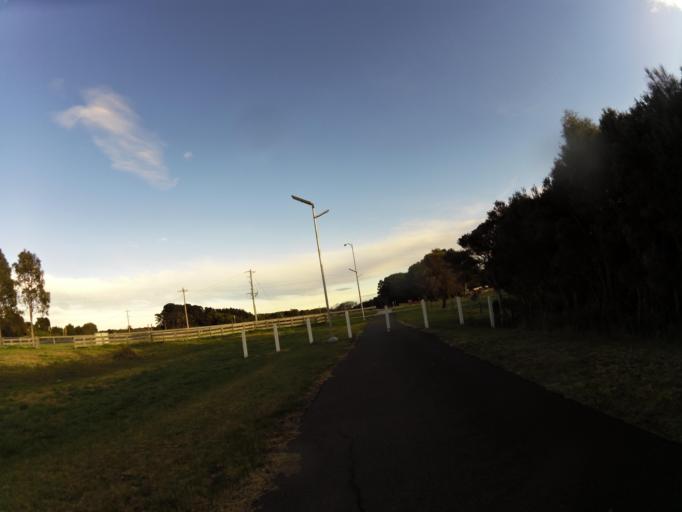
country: AU
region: Victoria
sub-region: Bass Coast
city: North Wonthaggi
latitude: -38.6045
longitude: 145.5792
